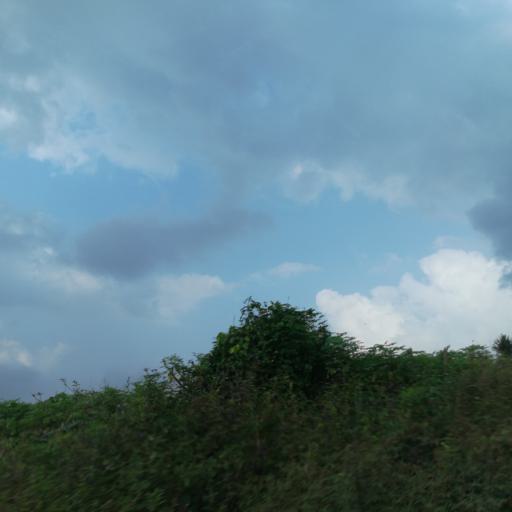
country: NG
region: Rivers
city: Okrika
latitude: 4.8246
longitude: 7.1253
